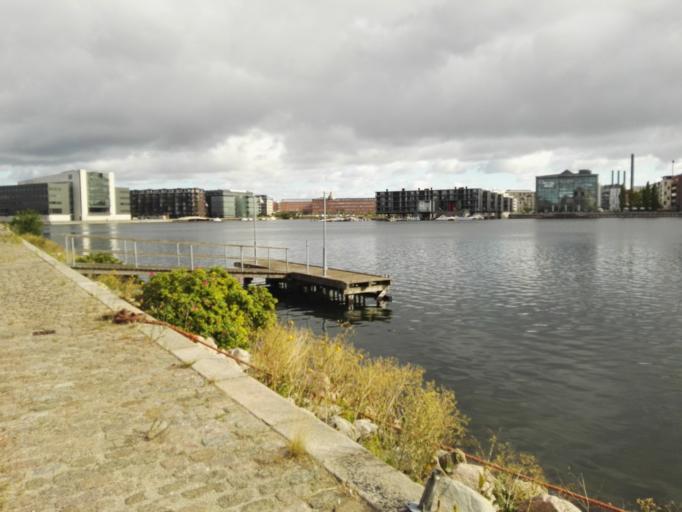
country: DK
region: Capital Region
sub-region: Frederiksberg Kommune
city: Frederiksberg
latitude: 55.6473
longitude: 12.5448
